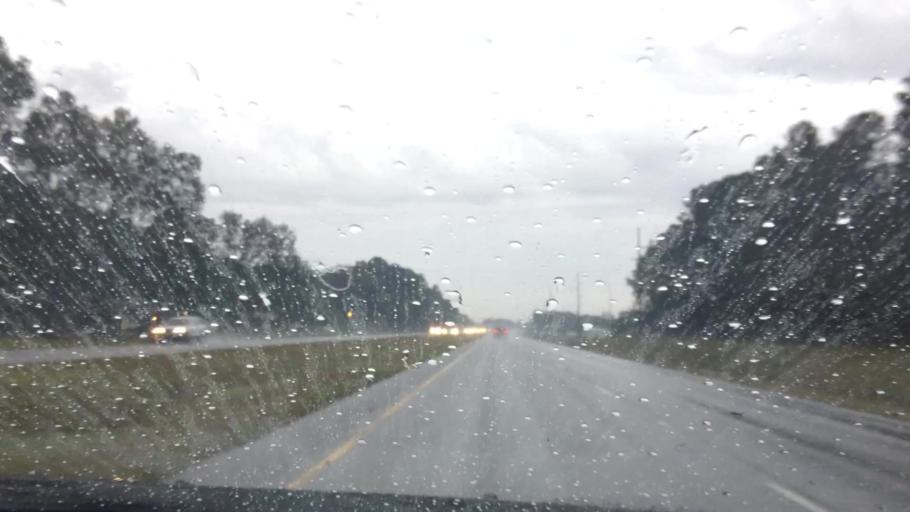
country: US
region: North Carolina
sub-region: Pitt County
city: Grifton
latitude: 35.4178
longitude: -77.4346
